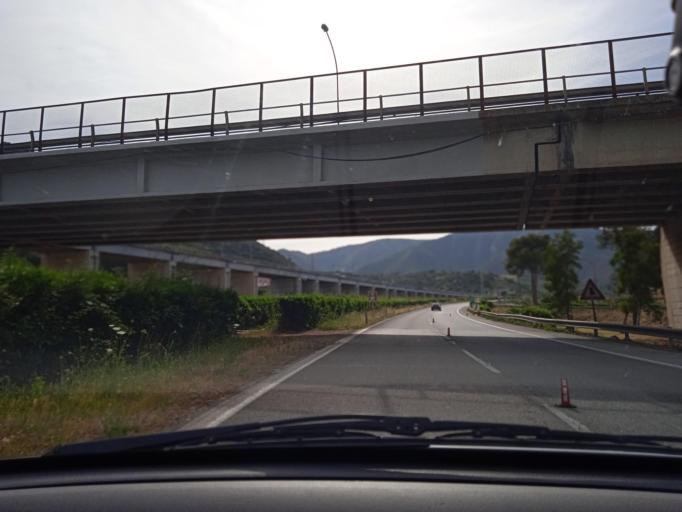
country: IT
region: Sicily
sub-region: Messina
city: Falcone
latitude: 38.1131
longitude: 15.0729
